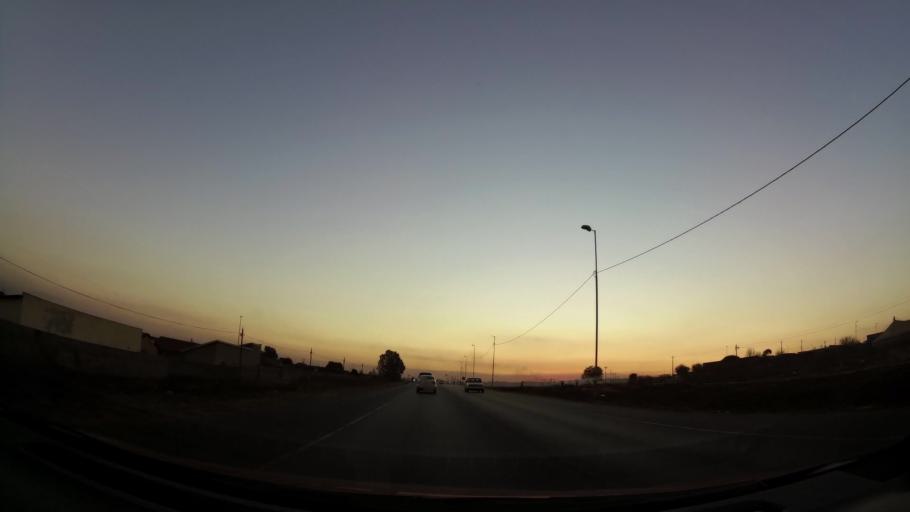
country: ZA
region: Gauteng
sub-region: City of Johannesburg Metropolitan Municipality
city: Soweto
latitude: -26.2312
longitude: 27.8204
